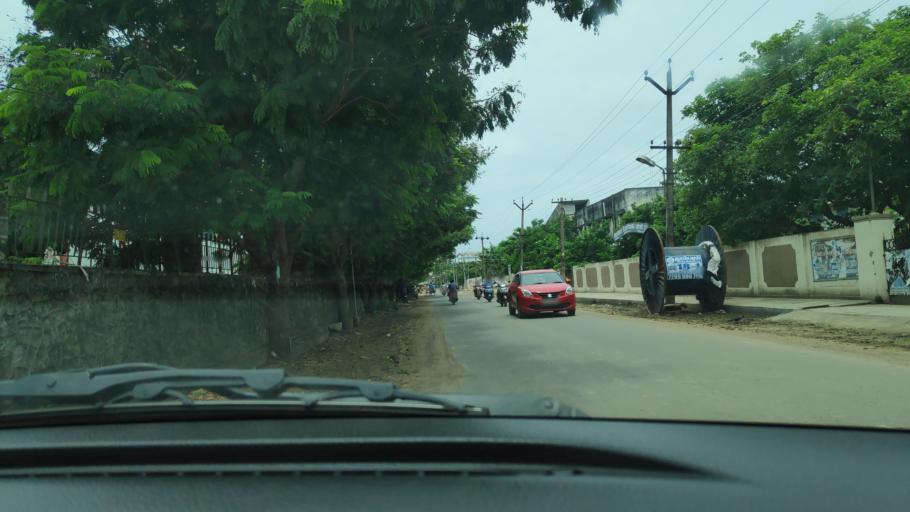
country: IN
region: Tamil Nadu
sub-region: Kancheepuram
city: Pallavaram
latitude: 12.9377
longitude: 80.1352
